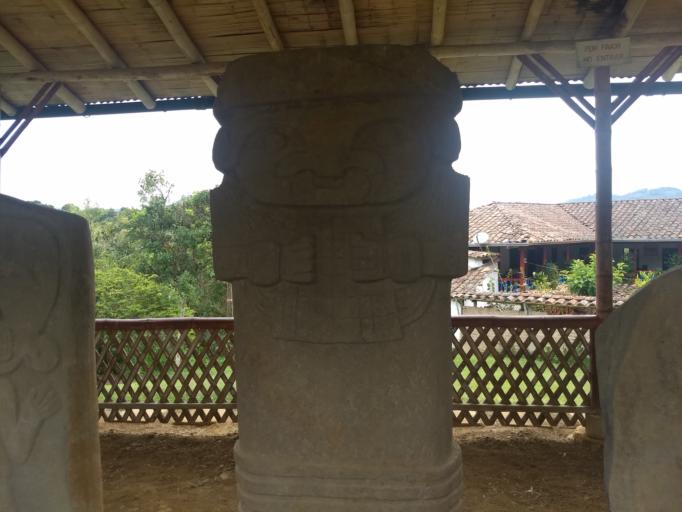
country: CO
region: Huila
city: San Agustin
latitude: 1.8991
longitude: -76.2751
